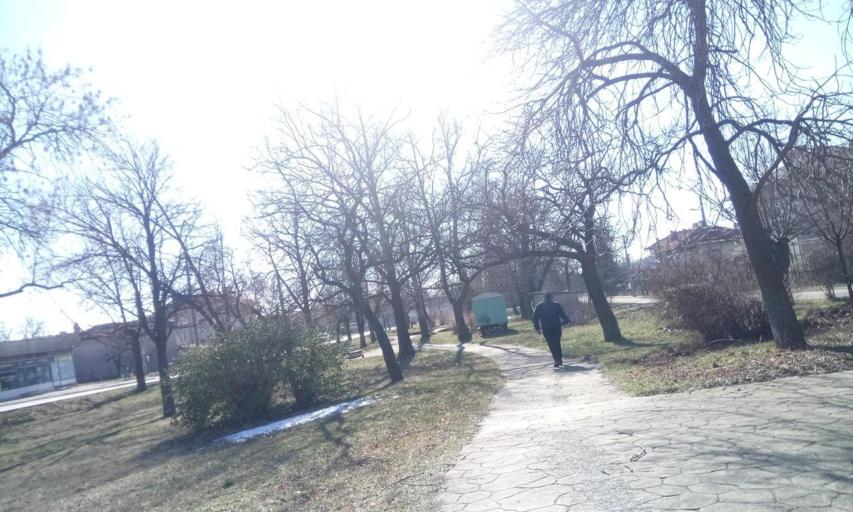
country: BG
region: Plovdiv
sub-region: Obshtina Khisarya
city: Khisarya
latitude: 42.5110
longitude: 24.7152
